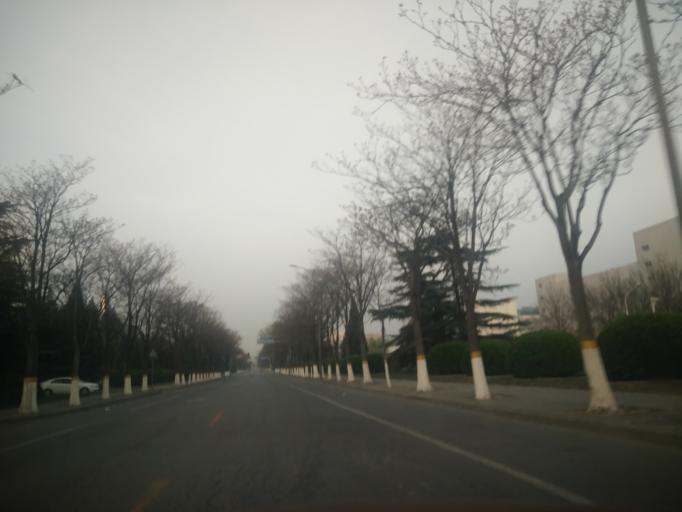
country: CN
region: Beijing
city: Jiugong
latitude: 39.8024
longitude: 116.5076
